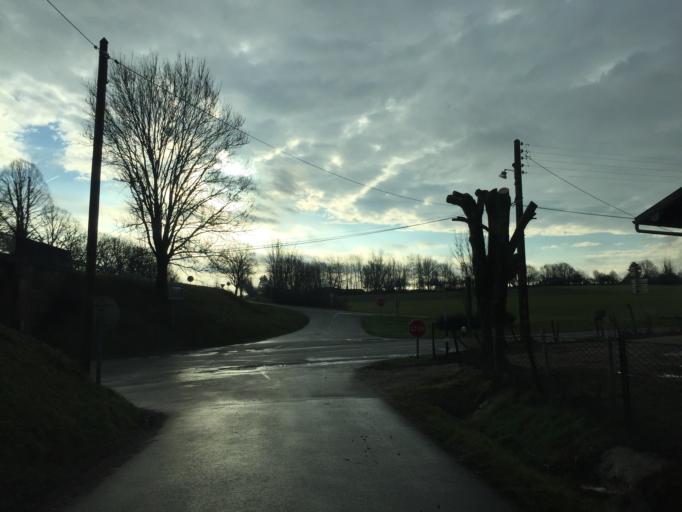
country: FR
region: Franche-Comte
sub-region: Departement du Jura
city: Mont-sous-Vaudrey
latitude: 46.9790
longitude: 5.5948
